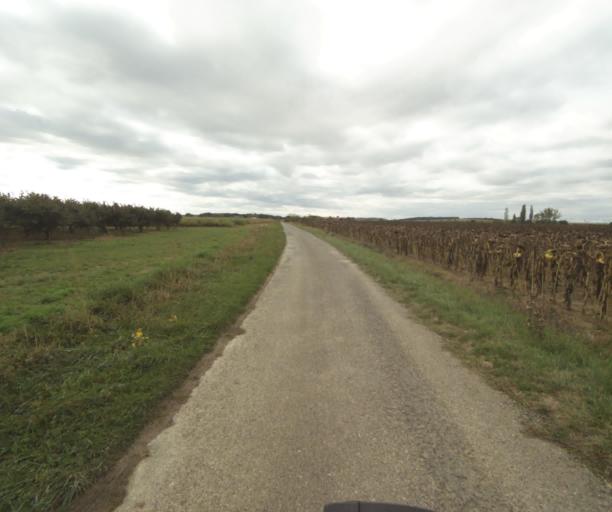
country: FR
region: Midi-Pyrenees
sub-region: Departement du Tarn-et-Garonne
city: Verdun-sur-Garonne
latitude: 43.8671
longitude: 1.1565
